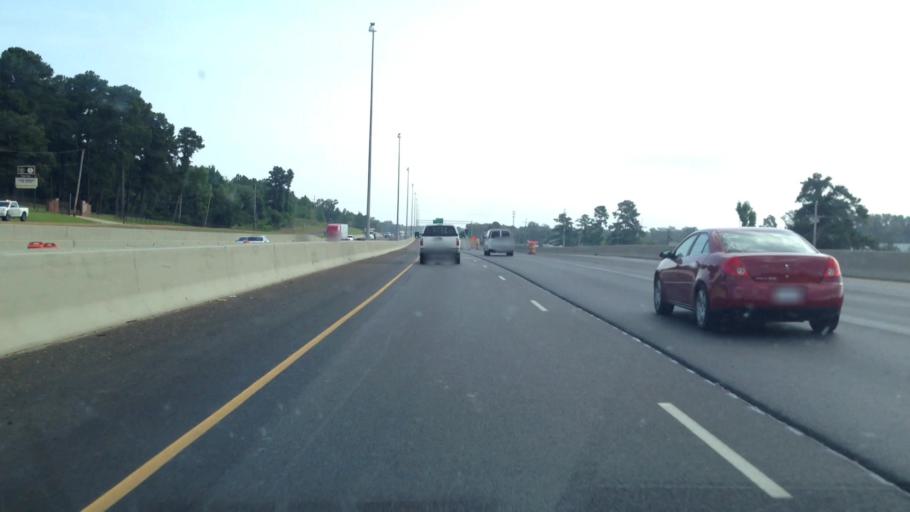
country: US
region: Mississippi
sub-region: Hinds County
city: Byram
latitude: 32.2238
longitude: -90.2245
